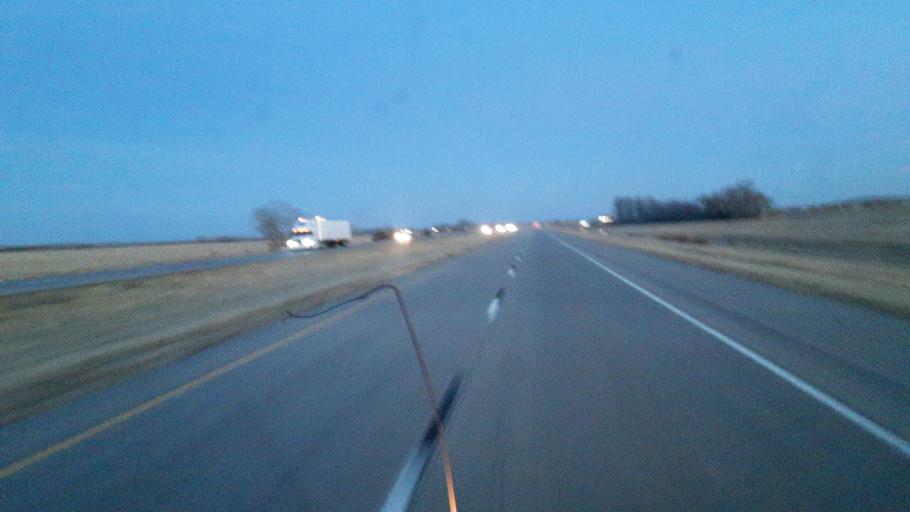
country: US
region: Nebraska
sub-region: Keith County
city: Ogallala
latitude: 41.1074
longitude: -101.4972
